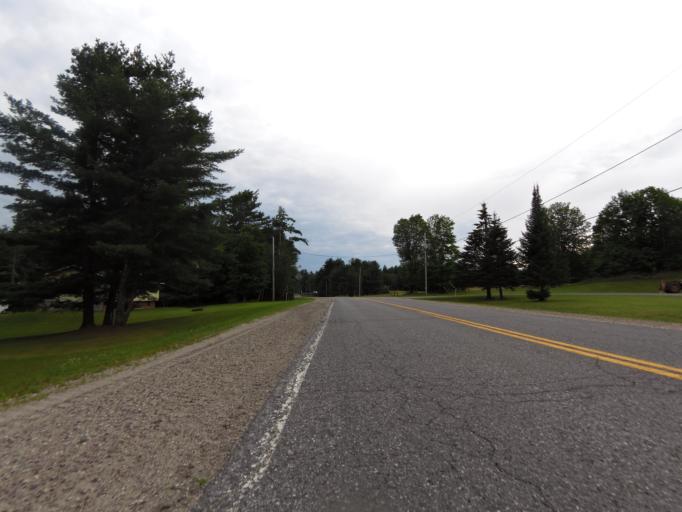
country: CA
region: Ontario
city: Carleton Place
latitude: 45.1179
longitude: -76.3527
